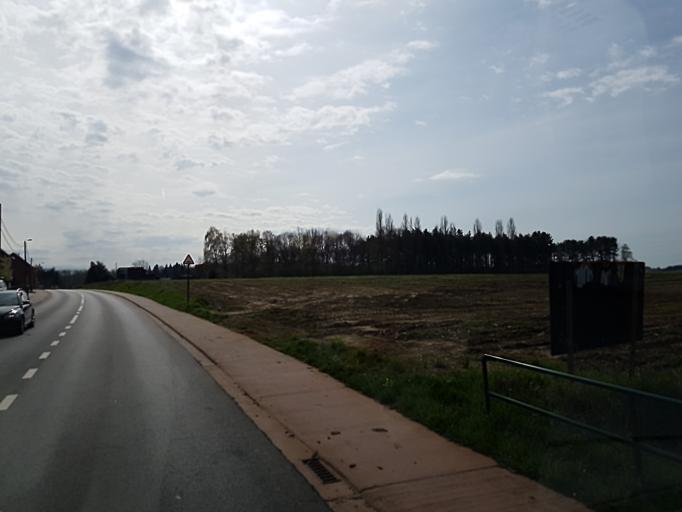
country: BE
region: Flanders
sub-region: Provincie Vlaams-Brabant
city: Scherpenheuvel-Zichem
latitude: 50.9963
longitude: 4.9946
